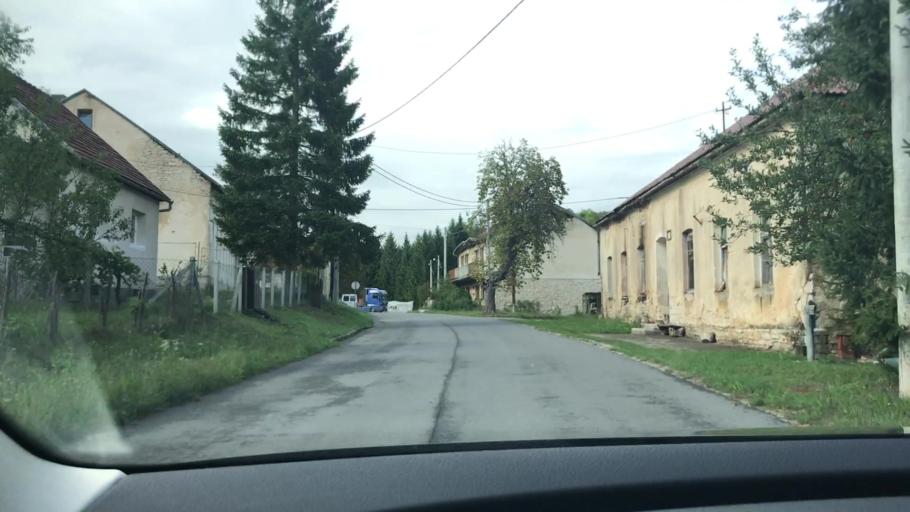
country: BA
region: Federation of Bosnia and Herzegovina
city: Izacic
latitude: 44.8790
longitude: 15.7123
